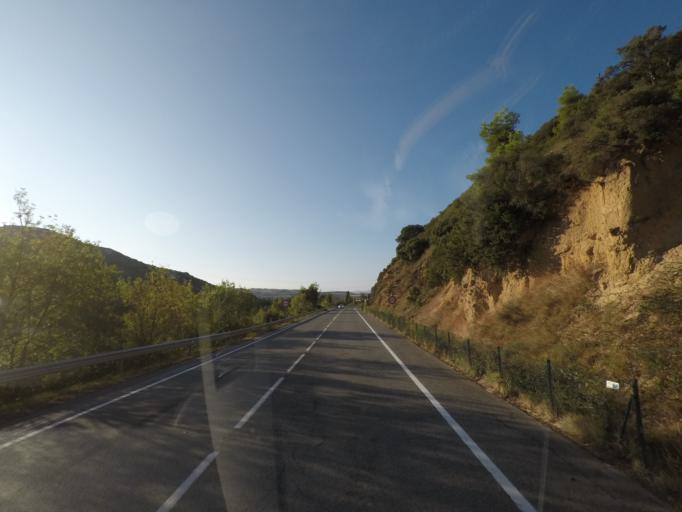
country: ES
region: Navarre
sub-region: Provincia de Navarra
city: Liedena
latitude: 42.6030
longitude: -1.2769
